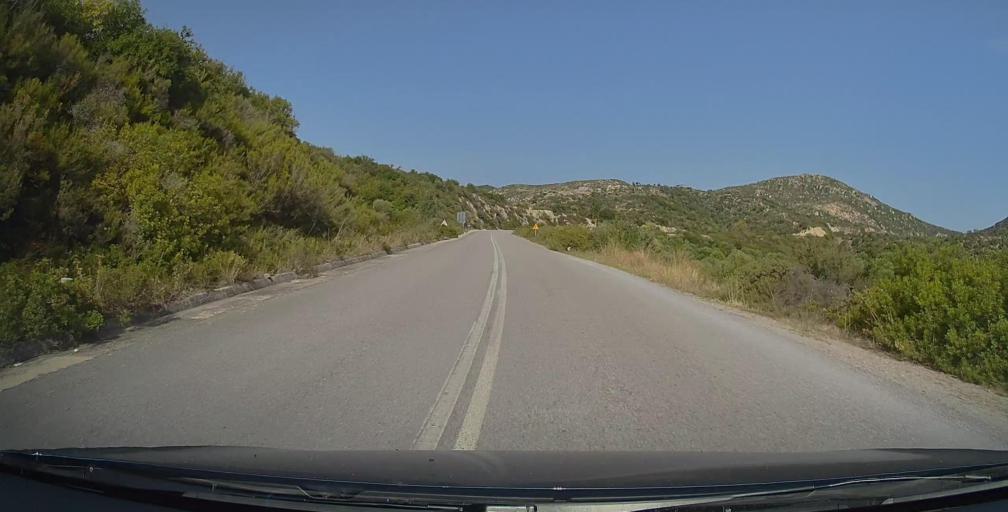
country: GR
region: Central Macedonia
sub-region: Nomos Chalkidikis
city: Sykia
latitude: 39.9937
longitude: 23.9901
